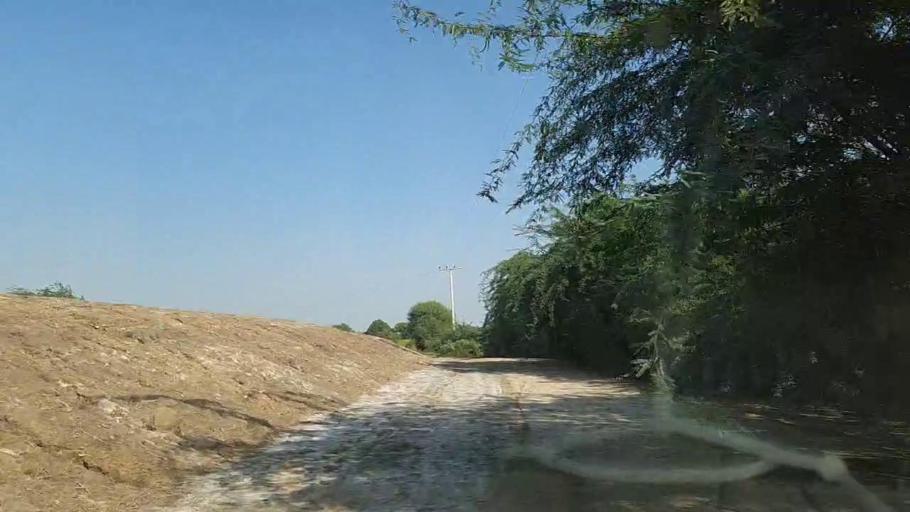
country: PK
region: Sindh
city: Chuhar Jamali
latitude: 24.5493
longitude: 68.0176
